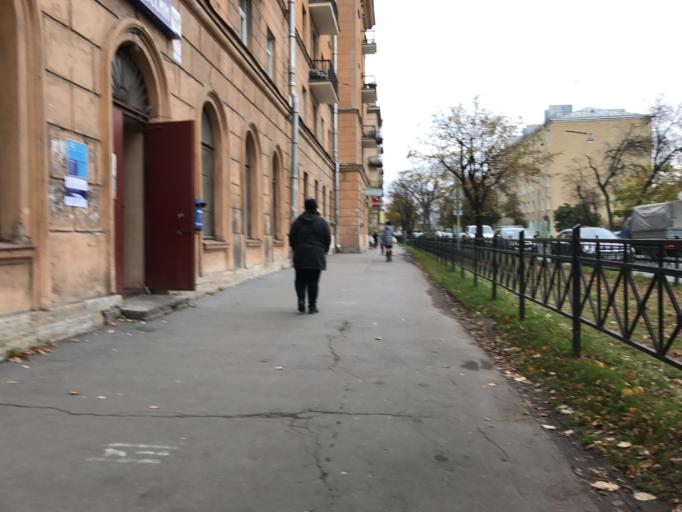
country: RU
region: St.-Petersburg
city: Obukhovo
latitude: 59.8976
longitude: 30.4267
